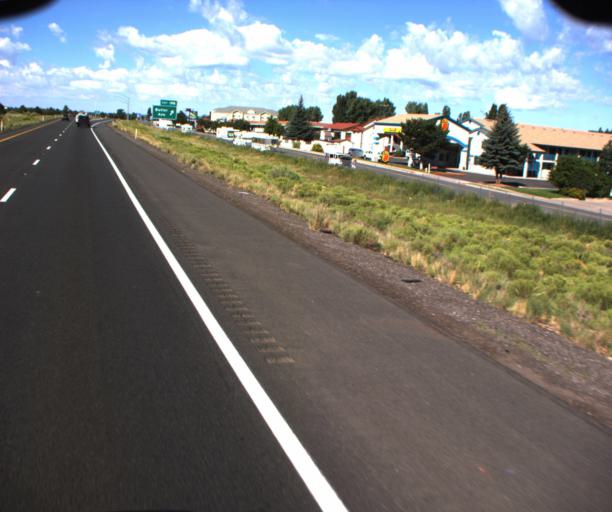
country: US
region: Arizona
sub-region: Coconino County
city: Flagstaff
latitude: 35.1957
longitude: -111.6169
